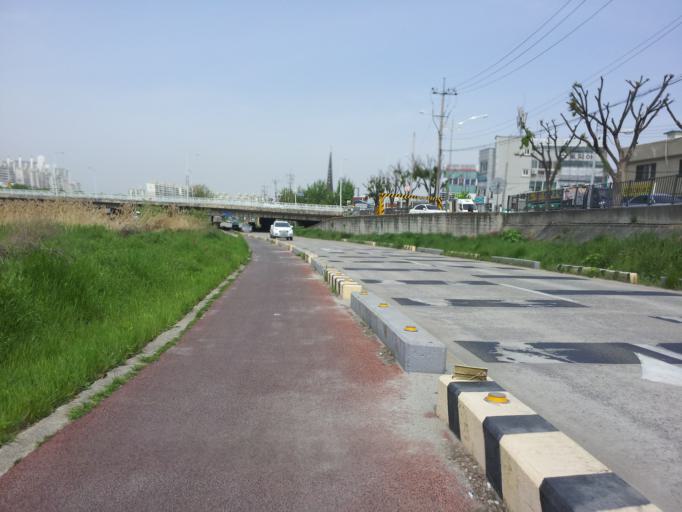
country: KR
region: Daejeon
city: Daejeon
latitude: 36.3384
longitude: 127.4204
